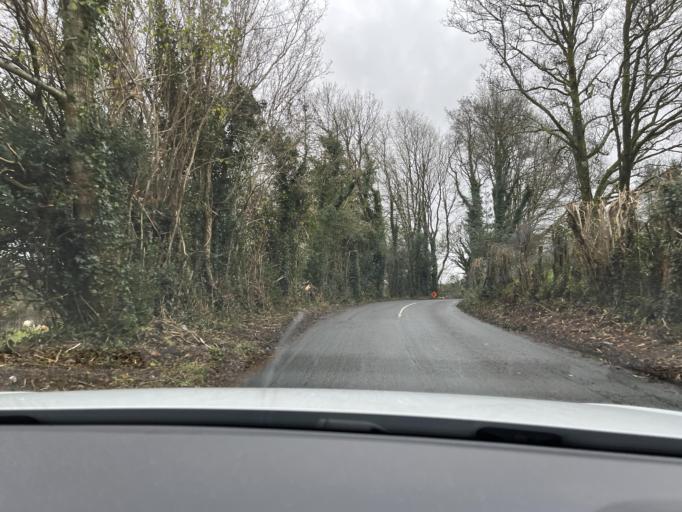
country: IE
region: Connaught
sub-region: County Leitrim
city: Manorhamilton
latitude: 54.2934
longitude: -8.2008
